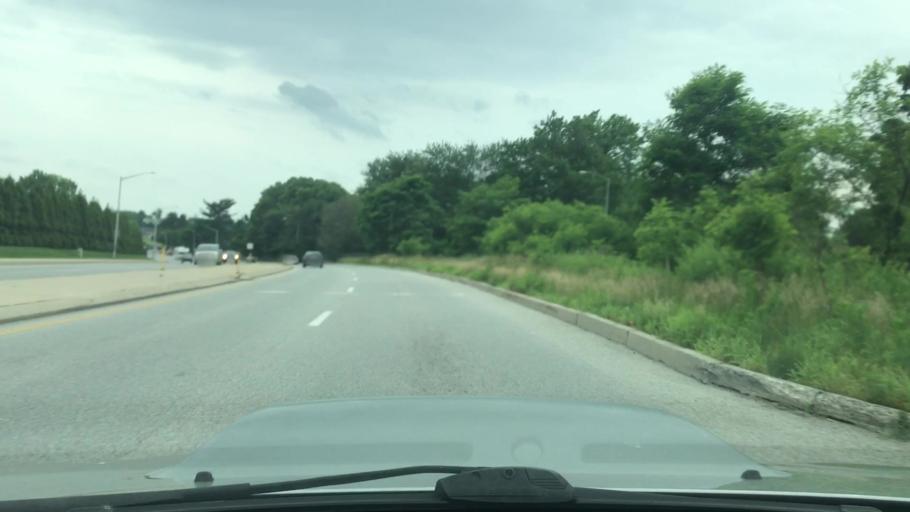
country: US
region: Pennsylvania
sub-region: Montgomery County
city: Wyncote
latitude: 40.0860
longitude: -75.1672
